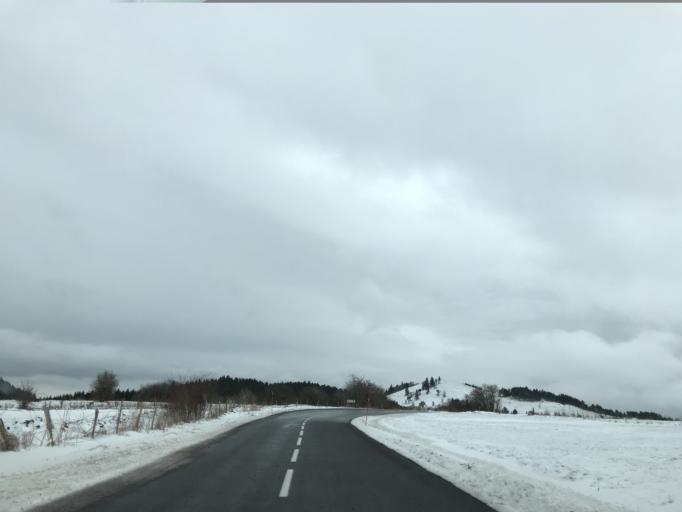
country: FR
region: Auvergne
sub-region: Departement du Puy-de-Dome
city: Aydat
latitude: 45.6743
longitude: 2.9361
